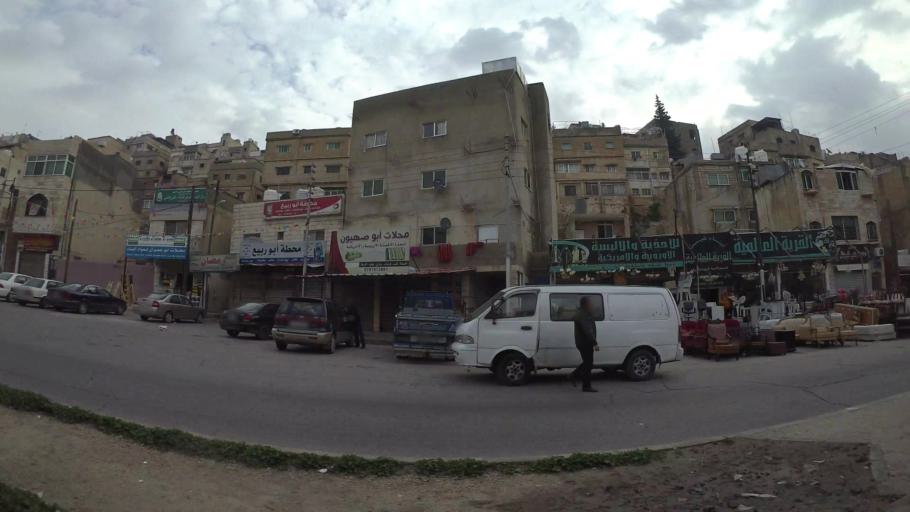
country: JO
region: Amman
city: Amman
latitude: 31.9657
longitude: 35.9269
